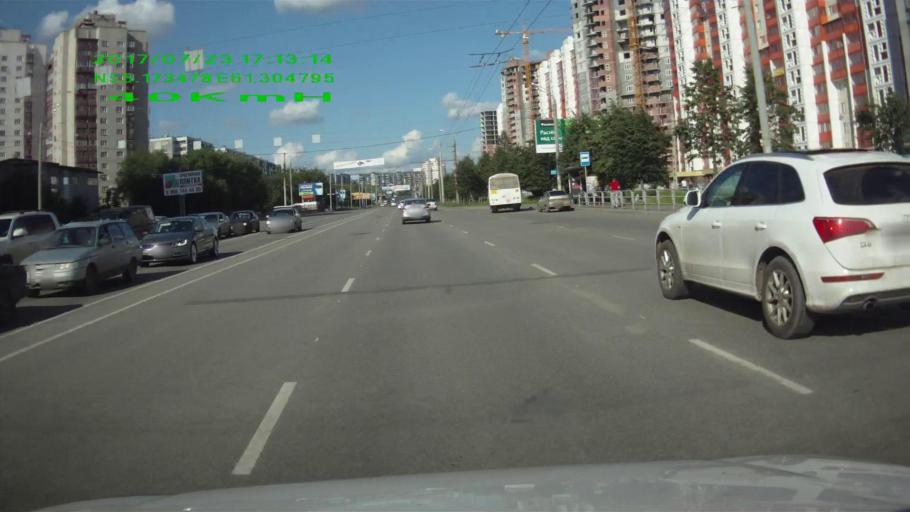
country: RU
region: Chelyabinsk
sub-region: Gorod Chelyabinsk
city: Chelyabinsk
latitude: 55.1737
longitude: 61.3053
